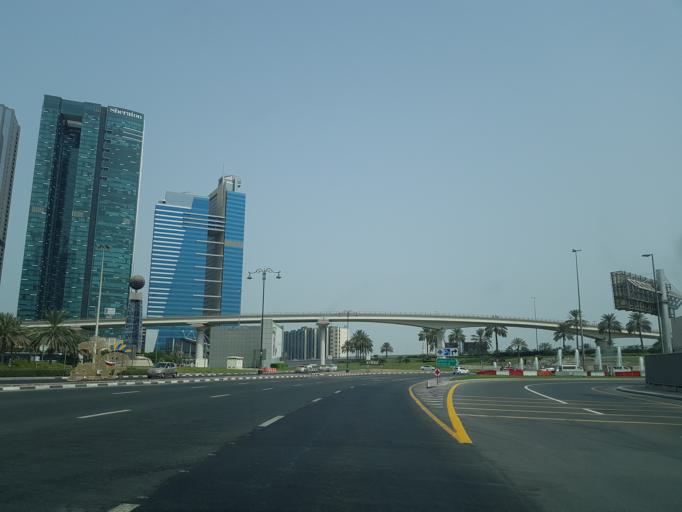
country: AE
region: Ash Shariqah
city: Sharjah
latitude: 25.2276
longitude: 55.2904
